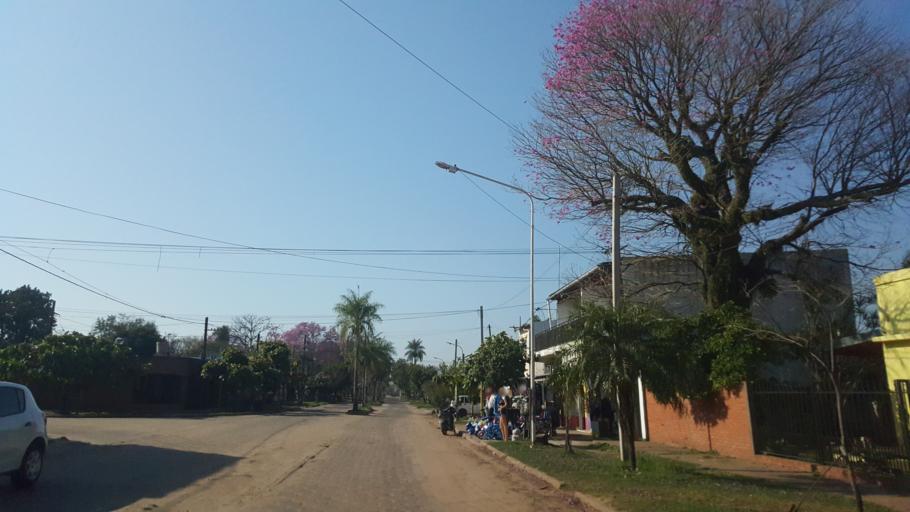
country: AR
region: Corrientes
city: Ituzaingo
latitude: -27.5909
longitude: -56.6888
